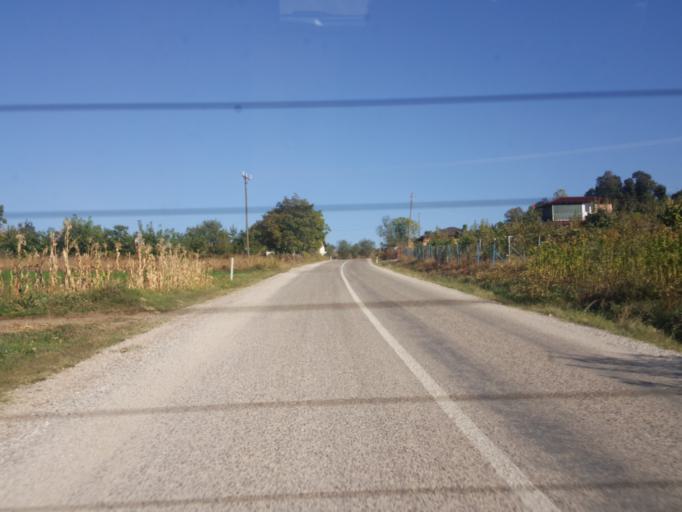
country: TR
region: Amasya
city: Tasova
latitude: 40.7135
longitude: 36.3257
